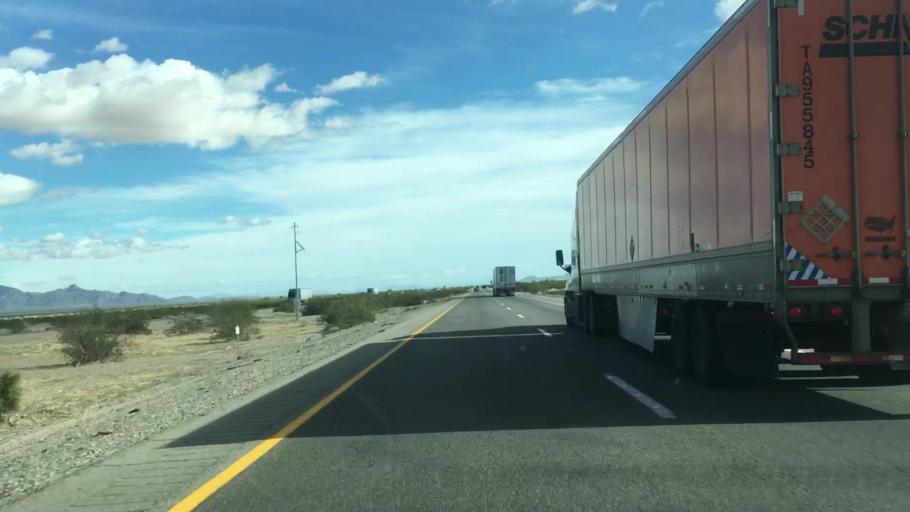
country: US
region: California
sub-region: Riverside County
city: Mesa Verde
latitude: 33.6283
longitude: -115.0658
